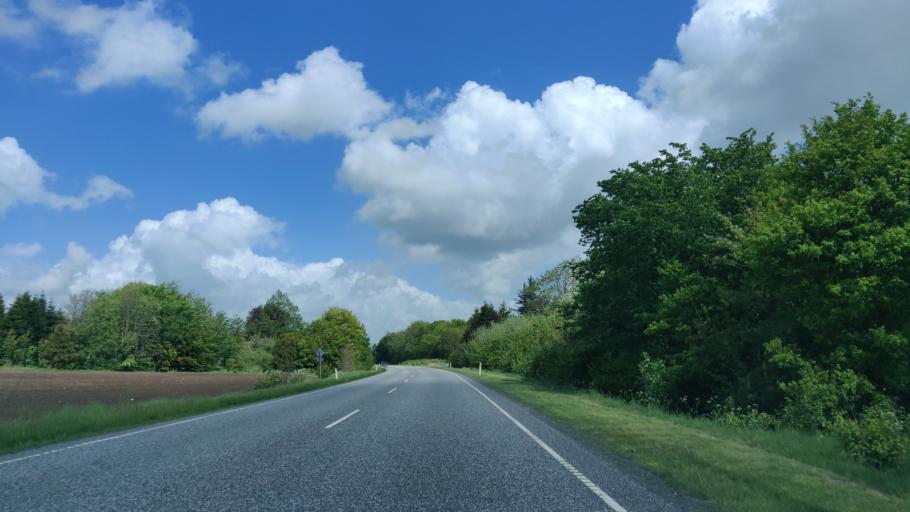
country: DK
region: Central Jutland
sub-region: Silkeborg Kommune
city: Kjellerup
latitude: 56.3346
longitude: 9.3408
